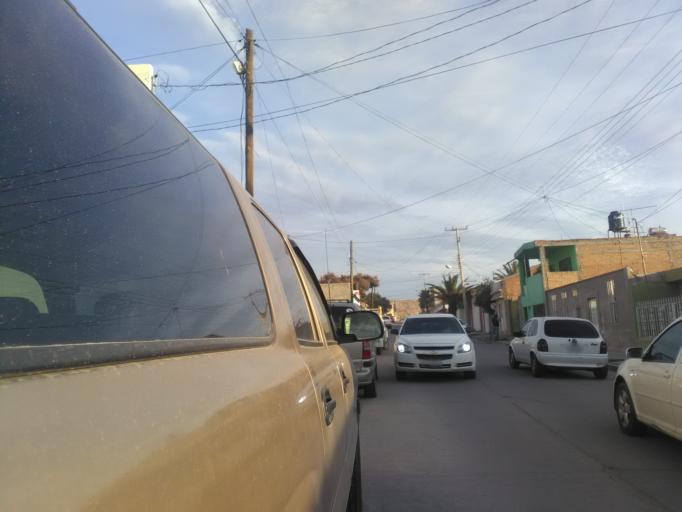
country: MX
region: Durango
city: Victoria de Durango
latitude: 24.0424
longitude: -104.6638
